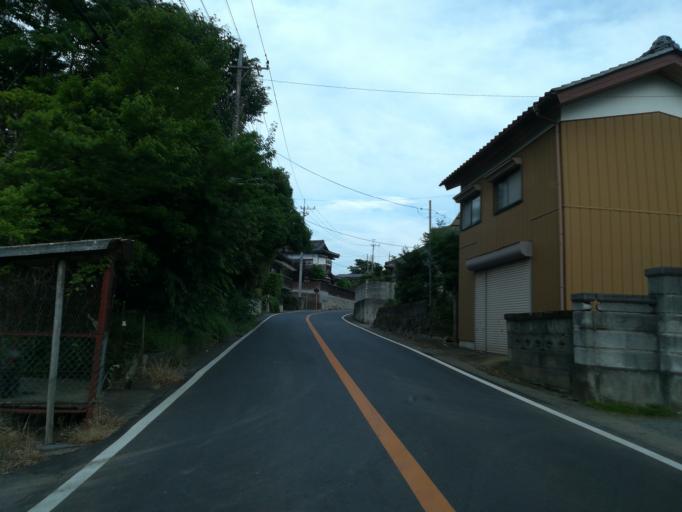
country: JP
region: Ibaraki
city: Tsukuba
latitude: 36.2244
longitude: 140.1535
